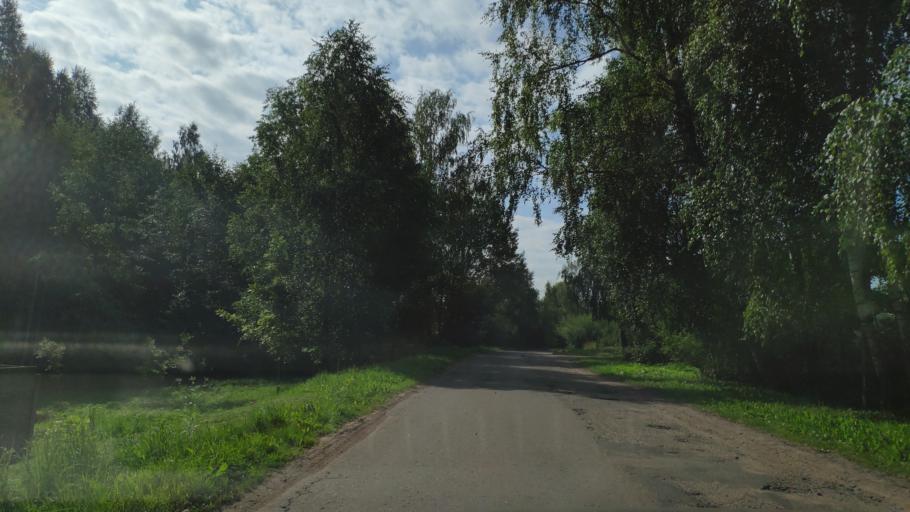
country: BY
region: Minsk
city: Zaslawye
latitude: 53.9865
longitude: 27.2887
